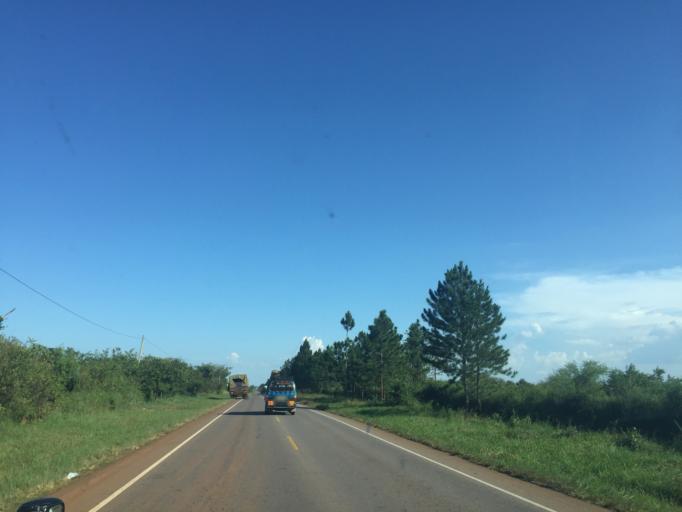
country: UG
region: Central Region
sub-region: Nakasongola District
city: Nakasongola
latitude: 1.3852
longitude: 32.3320
